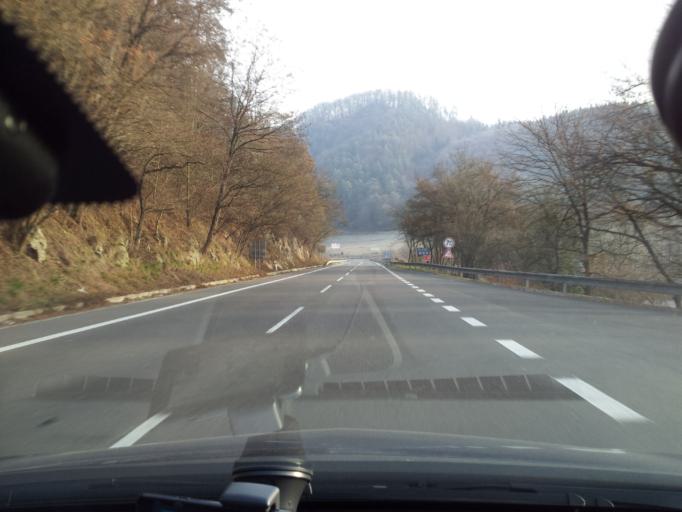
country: SK
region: Banskobystricky
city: Hrochot,Slovakia
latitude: 48.7802
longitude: 19.3341
